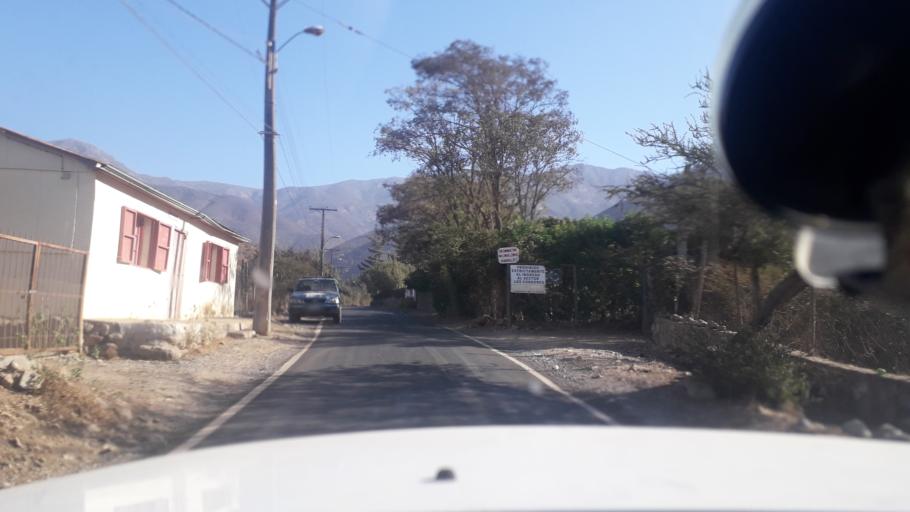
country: CL
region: Valparaiso
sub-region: Provincia de Marga Marga
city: Limache
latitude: -33.0556
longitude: -71.1127
